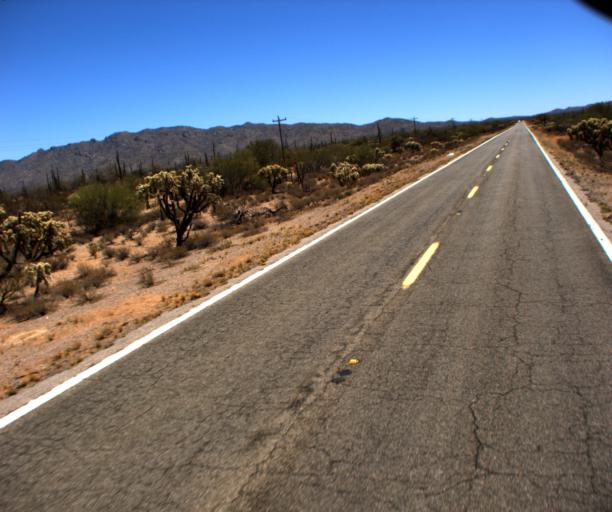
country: US
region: Arizona
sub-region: Pima County
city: Sells
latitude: 32.1829
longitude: -112.2993
